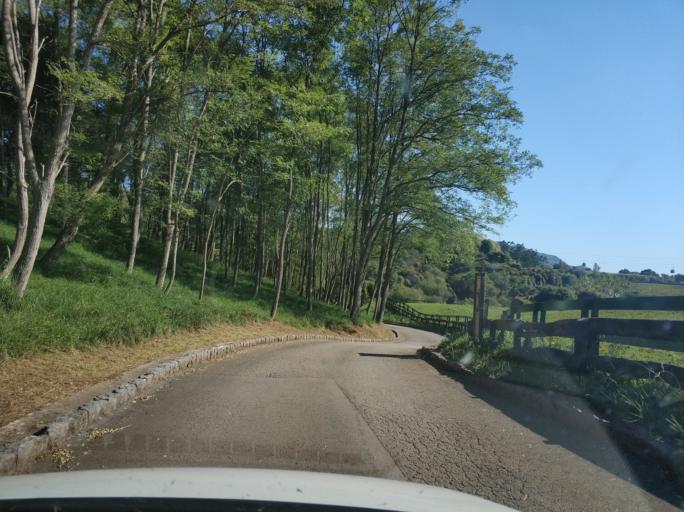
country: ES
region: Cantabria
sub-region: Provincia de Cantabria
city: Penagos
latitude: 43.3517
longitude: -3.8453
